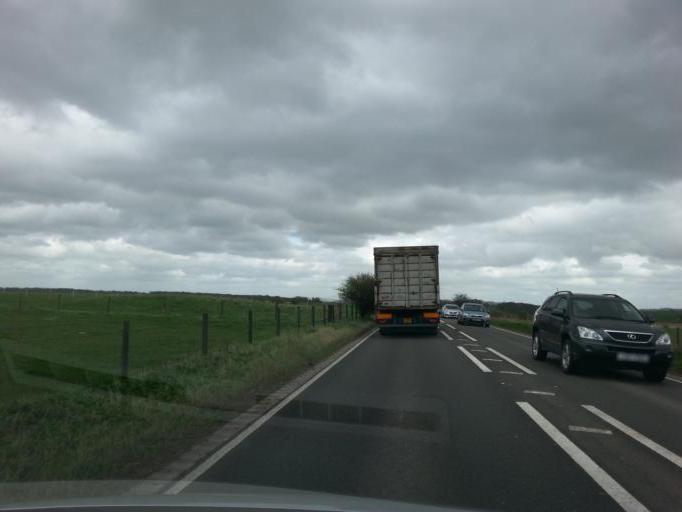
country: GB
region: England
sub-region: Wiltshire
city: Durnford
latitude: 51.1753
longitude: -1.8366
